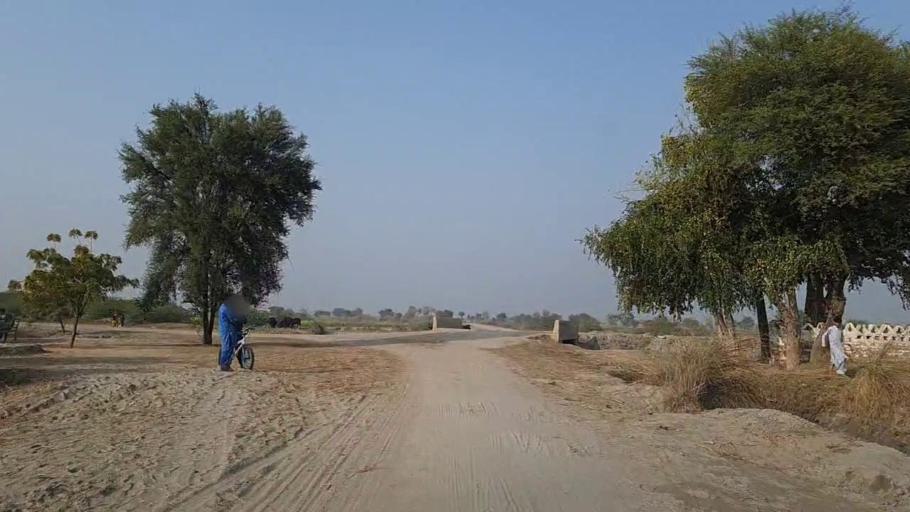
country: PK
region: Sindh
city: Nawabshah
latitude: 26.3424
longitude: 68.4893
